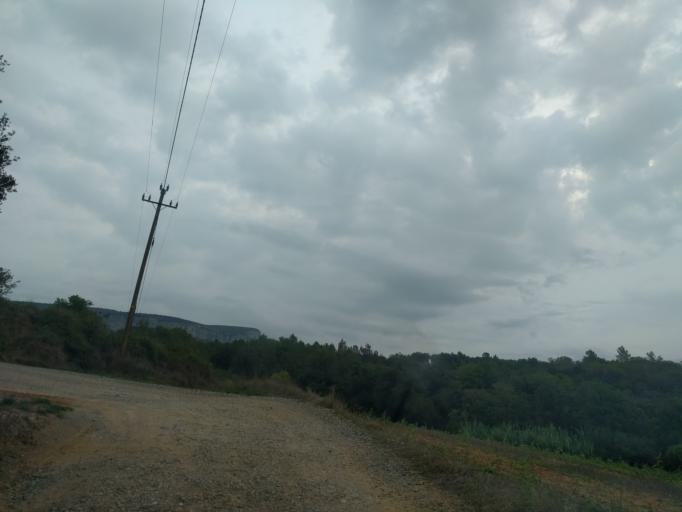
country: ES
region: Catalonia
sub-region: Provincia de Girona
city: la Cellera de Ter
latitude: 42.0032
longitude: 2.6326
